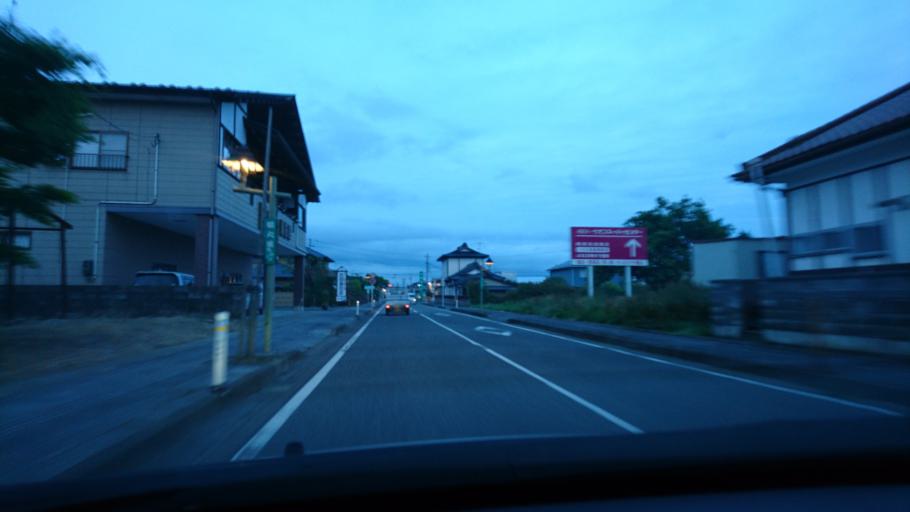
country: JP
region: Iwate
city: Ichinoseki
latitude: 38.8321
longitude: 140.9931
